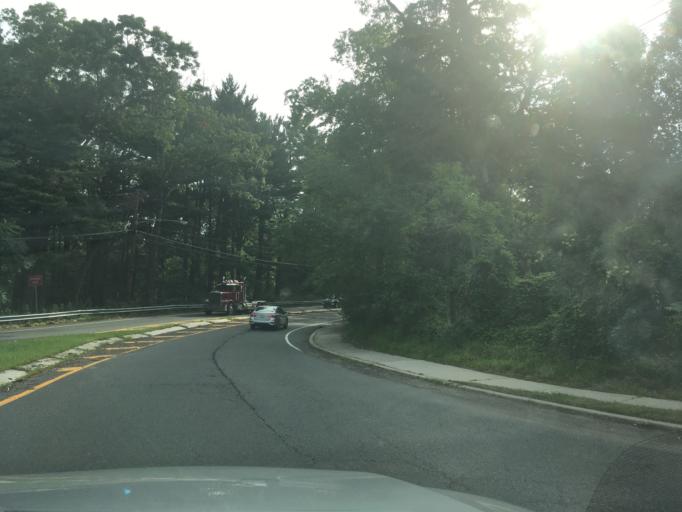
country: US
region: New Jersey
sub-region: Mercer County
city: Princeton Junction
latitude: 40.3201
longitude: -74.6233
